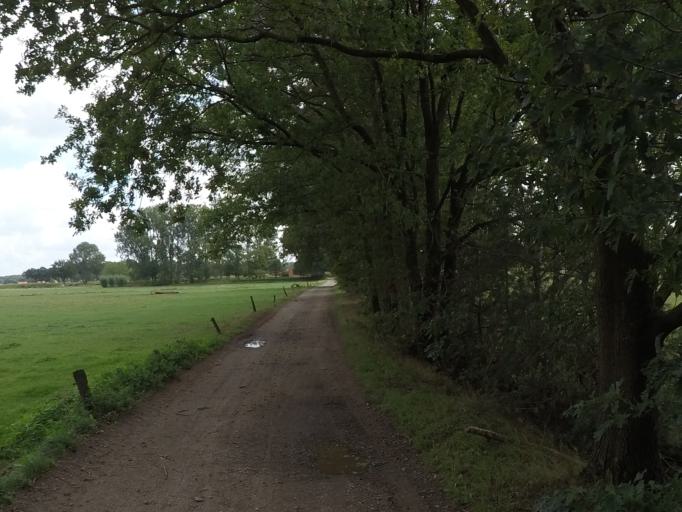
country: BE
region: Flanders
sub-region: Provincie Antwerpen
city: Grobbendonk
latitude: 51.2143
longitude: 4.7310
